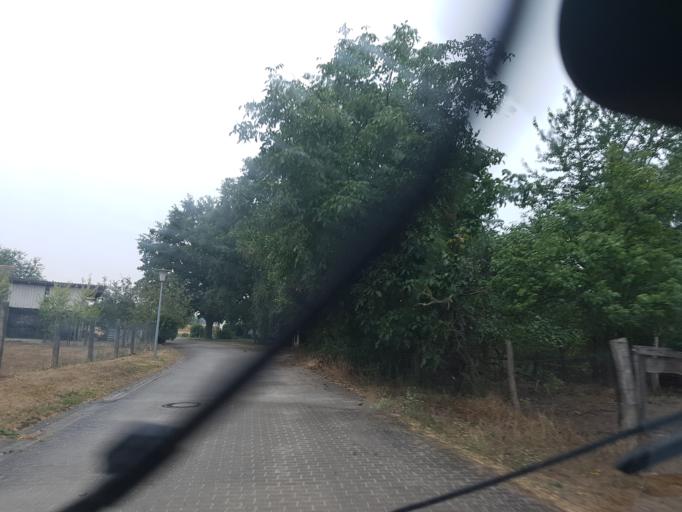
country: DE
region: Brandenburg
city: Niemegk
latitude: 52.0540
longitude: 12.6257
